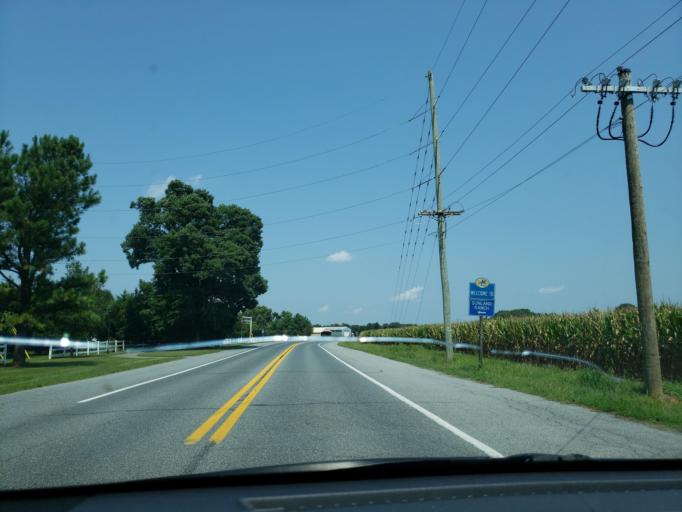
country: US
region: Delaware
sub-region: Sussex County
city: Milton
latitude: 38.8054
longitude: -75.3154
